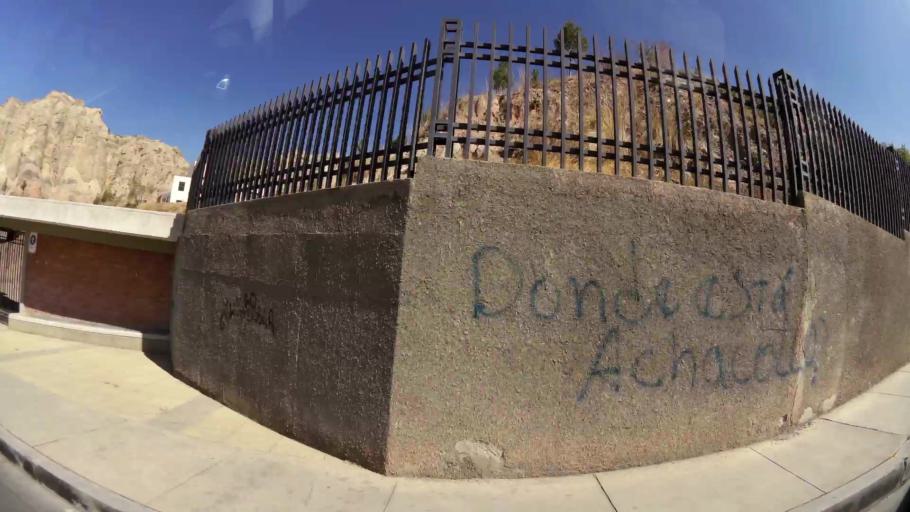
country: BO
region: La Paz
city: La Paz
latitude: -16.5244
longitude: -68.0908
